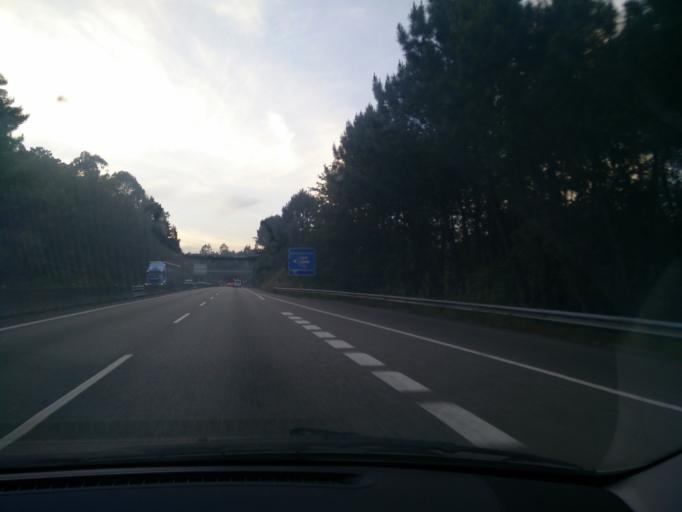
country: ES
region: Galicia
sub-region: Provincia de Pontevedra
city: Porrino
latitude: 42.1770
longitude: -8.6250
